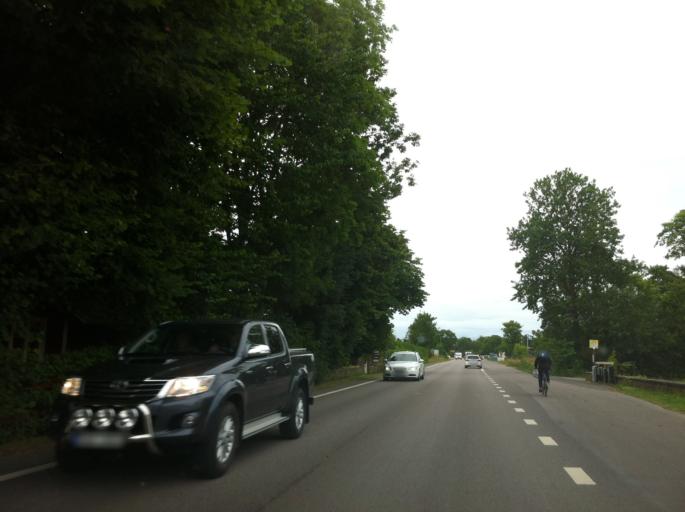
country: SE
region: Kalmar
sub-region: Borgholms Kommun
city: Borgholm
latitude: 57.2454
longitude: 17.0596
